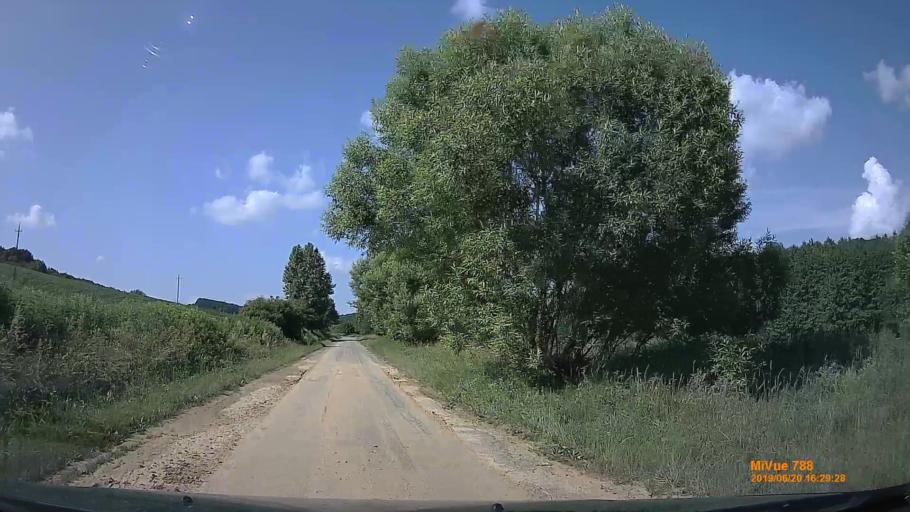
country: HU
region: Baranya
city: Buekkoesd
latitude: 46.1614
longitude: 18.0586
